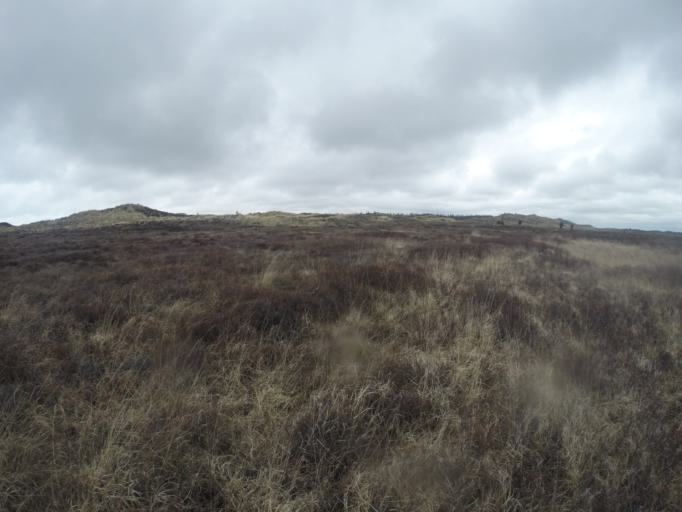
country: DK
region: North Denmark
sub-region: Thisted Kommune
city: Hurup
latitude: 56.8969
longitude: 8.3342
